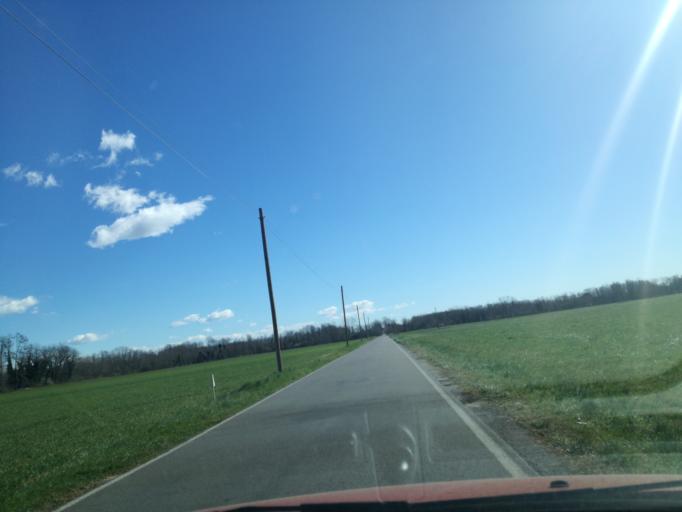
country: IT
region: Lombardy
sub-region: Provincia di Monza e Brianza
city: Burago di Molgora
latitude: 45.6047
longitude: 9.3956
